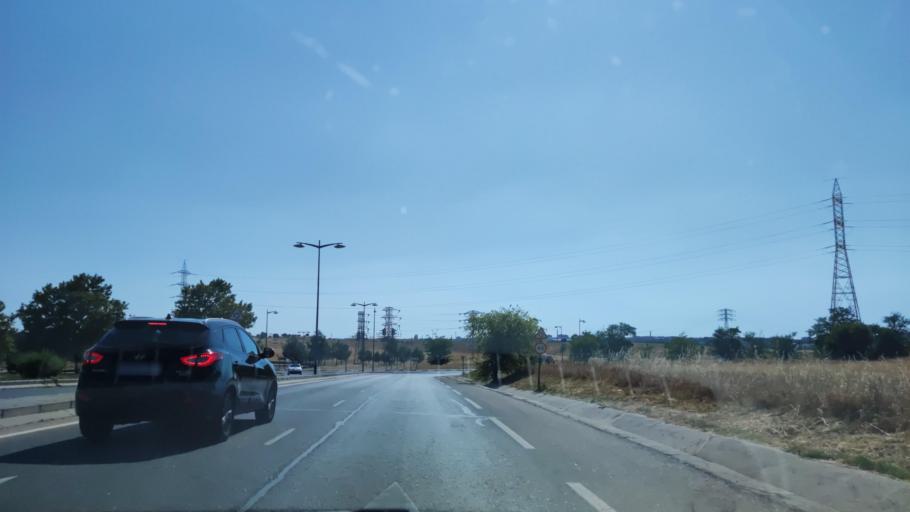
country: ES
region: Madrid
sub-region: Provincia de Madrid
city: Leganes
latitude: 40.3449
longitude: -3.7842
